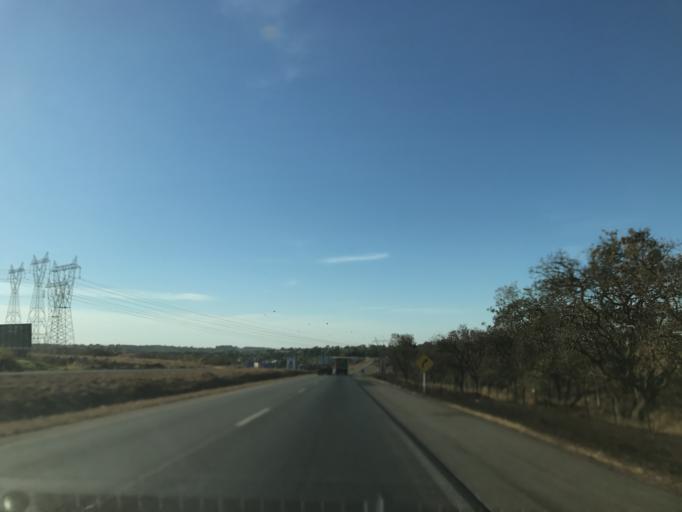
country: BR
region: Goias
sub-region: Hidrolandia
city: Hidrolandia
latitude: -16.9521
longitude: -49.2449
